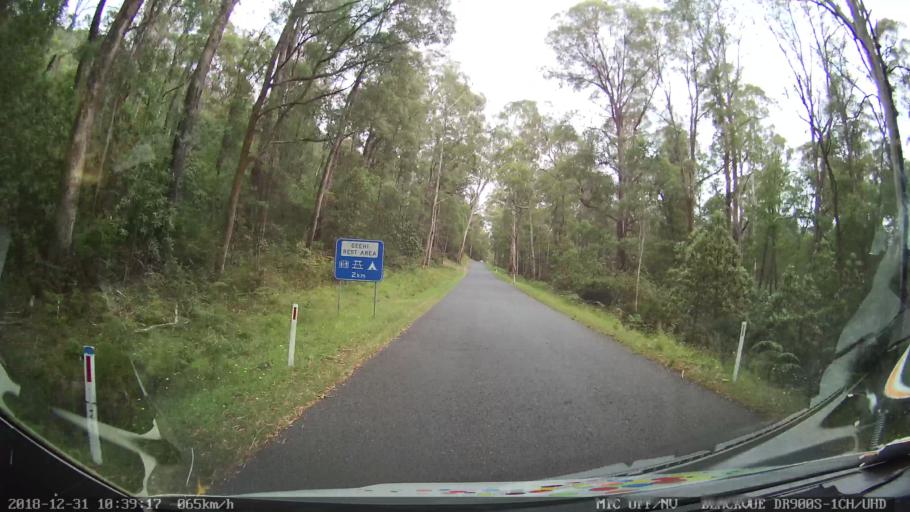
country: AU
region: New South Wales
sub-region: Snowy River
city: Jindabyne
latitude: -36.4006
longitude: 148.1770
